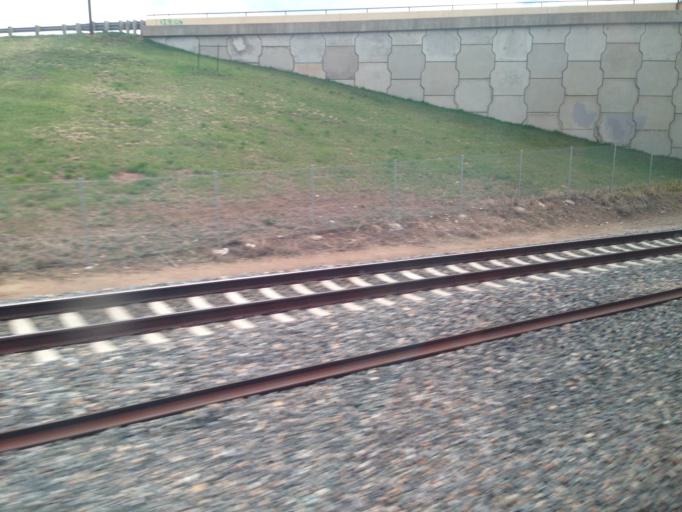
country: US
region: Colorado
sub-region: Jefferson County
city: Arvada
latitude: 39.8011
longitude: -105.0602
